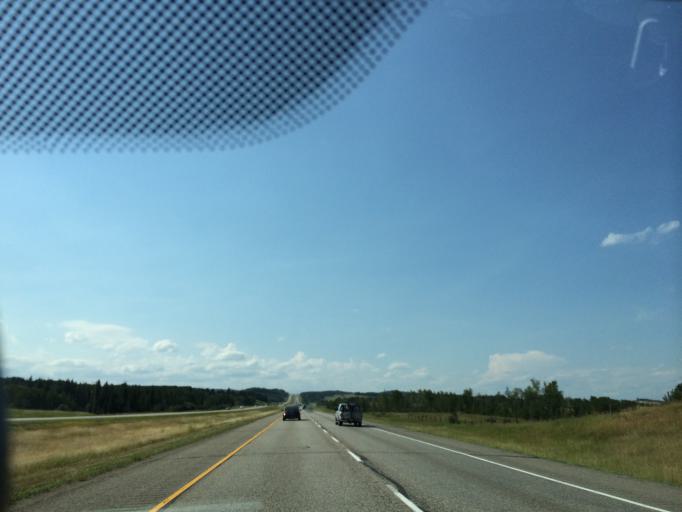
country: CA
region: Alberta
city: Cochrane
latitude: 51.1225
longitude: -114.6719
